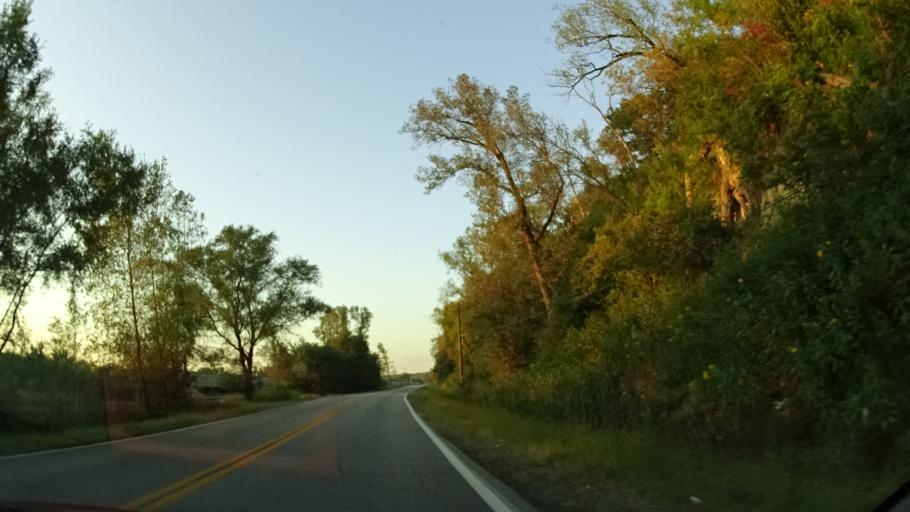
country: US
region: Iowa
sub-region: Pottawattamie County
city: Council Bluffs
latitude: 41.2786
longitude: -95.8601
